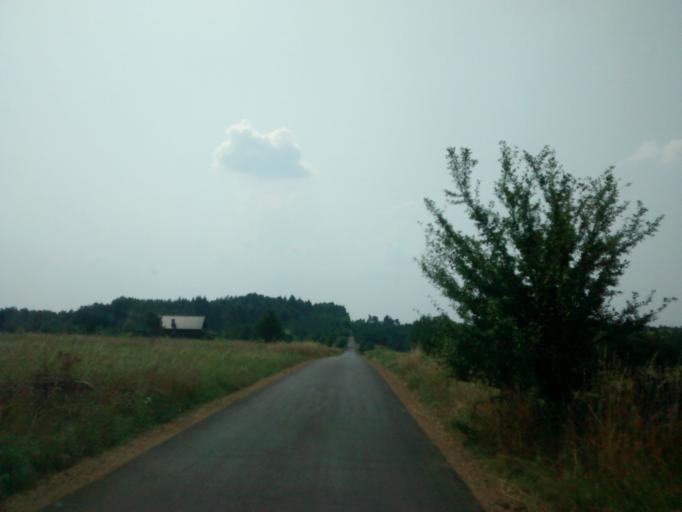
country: PL
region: Lesser Poland Voivodeship
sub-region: Powiat olkuski
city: Klucze
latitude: 50.3658
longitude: 19.5233
